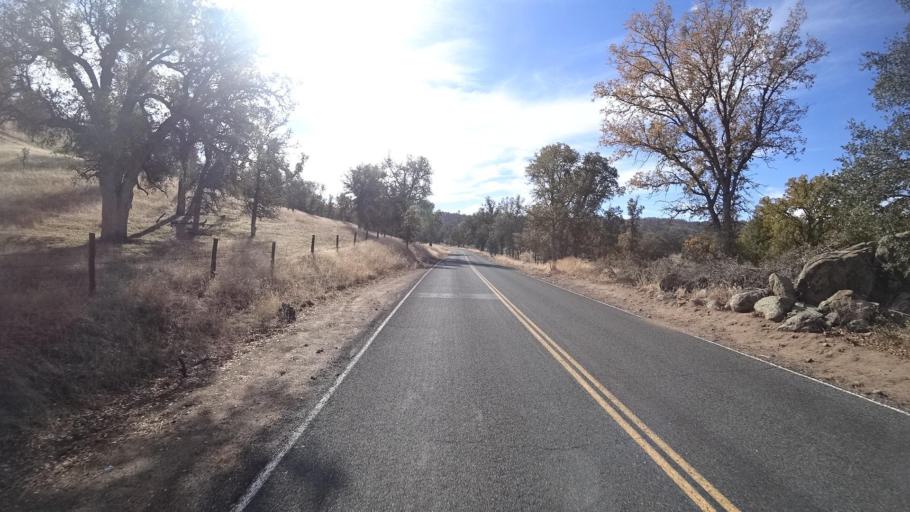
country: US
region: California
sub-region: Kern County
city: Alta Sierra
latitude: 35.6667
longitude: -118.7461
